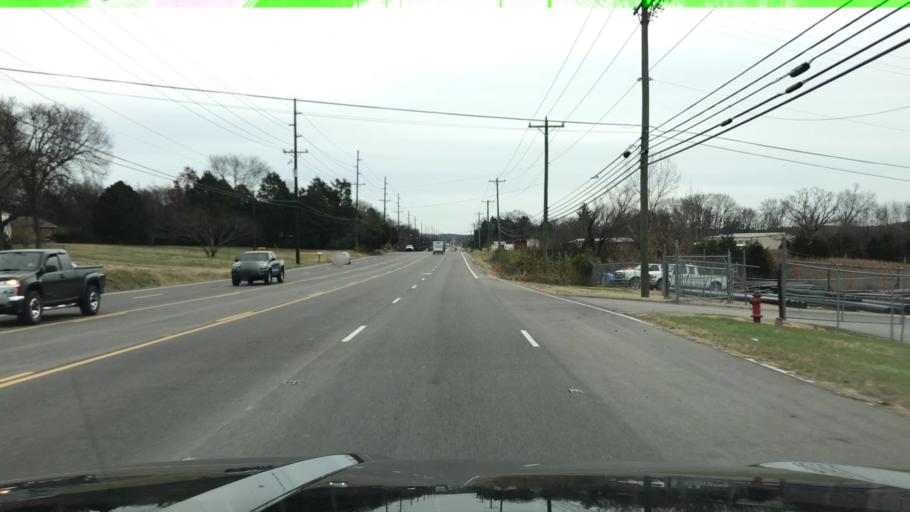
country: US
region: Tennessee
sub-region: Rutherford County
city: La Vergne
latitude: 36.0383
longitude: -86.6018
